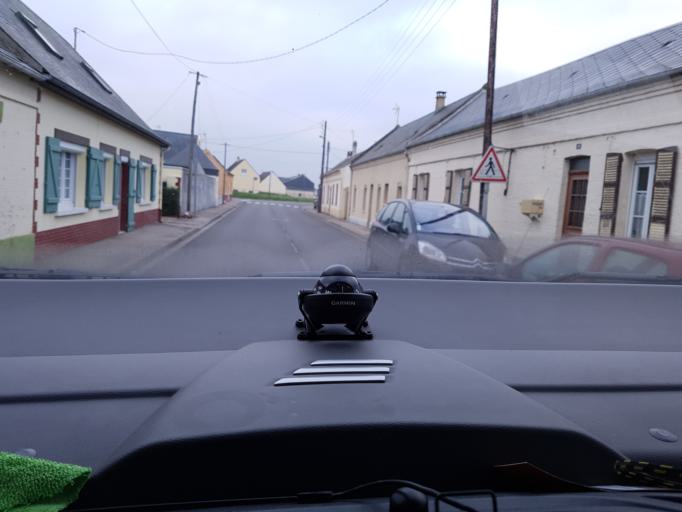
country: FR
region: Picardie
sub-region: Departement de la Somme
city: Cayeux-sur-Mer
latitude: 50.1723
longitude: 1.4956
